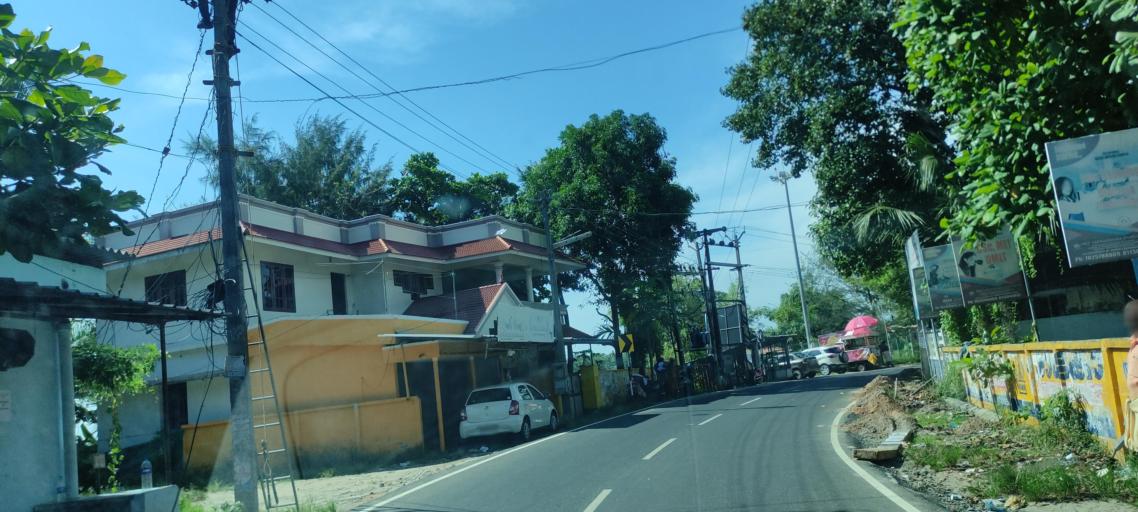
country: IN
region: Kerala
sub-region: Alappuzha
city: Mavelikara
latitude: 9.3107
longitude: 76.3840
